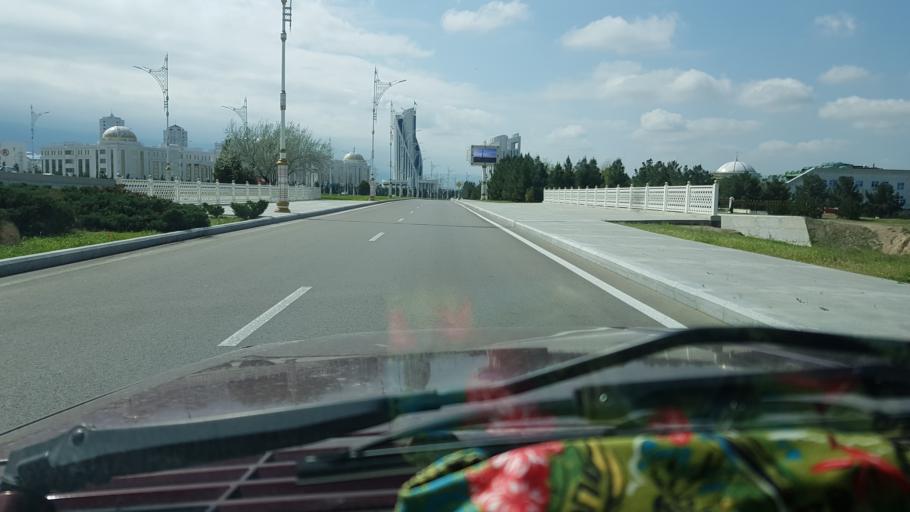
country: TM
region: Ahal
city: Ashgabat
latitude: 37.8797
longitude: 58.3728
